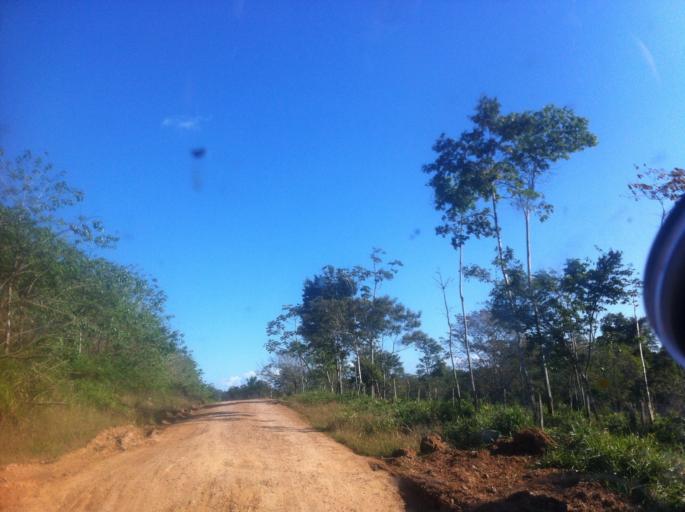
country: CR
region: Alajuela
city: Los Chiles
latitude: 11.0572
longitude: -84.4849
